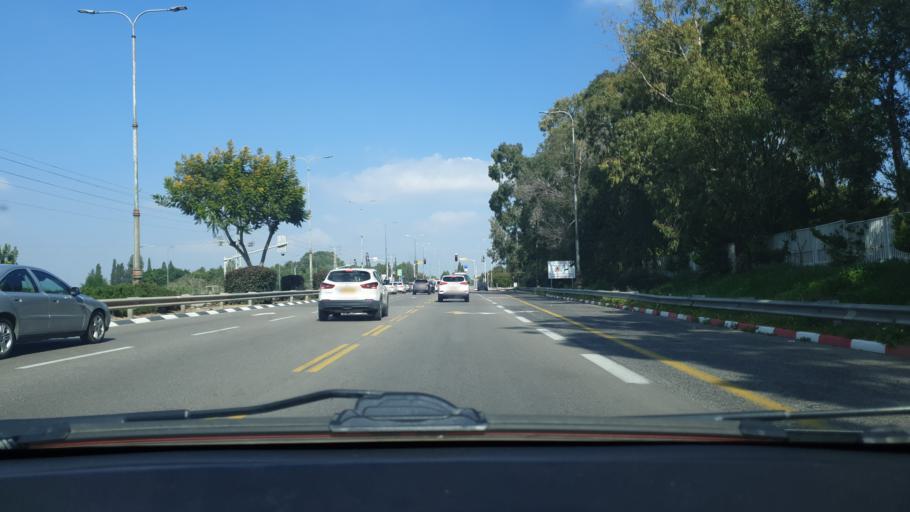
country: IL
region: Central District
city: Bet Dagan
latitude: 31.9919
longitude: 34.8133
